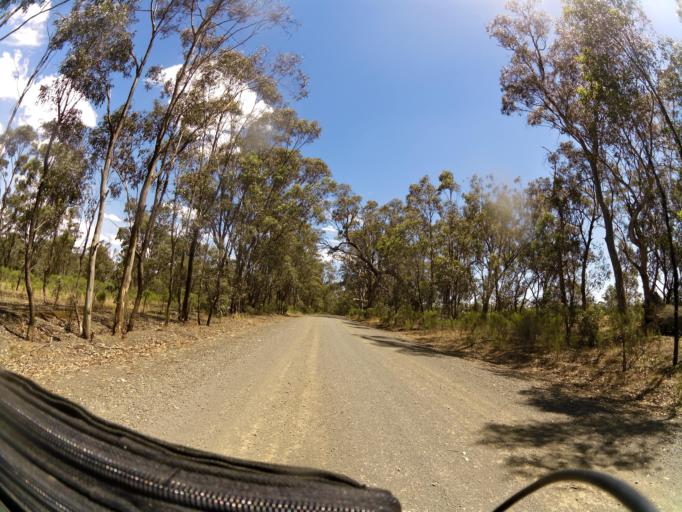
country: AU
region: Victoria
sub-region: Campaspe
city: Kyabram
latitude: -36.7999
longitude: 145.0781
